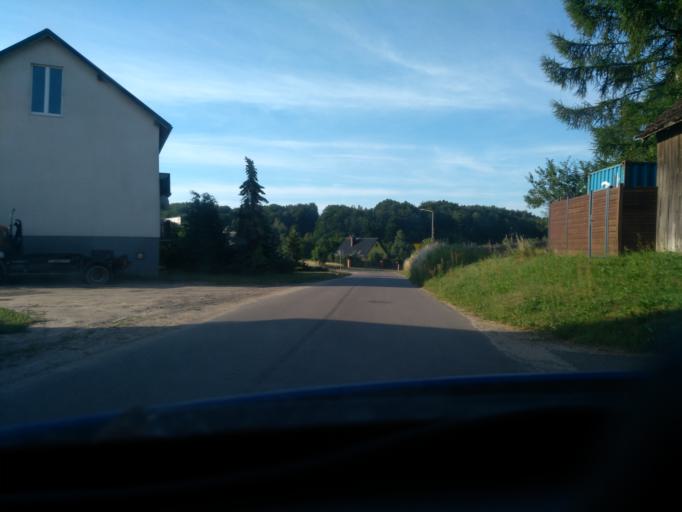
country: PL
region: Pomeranian Voivodeship
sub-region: Powiat kartuski
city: Przodkowo
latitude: 54.3815
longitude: 18.3172
